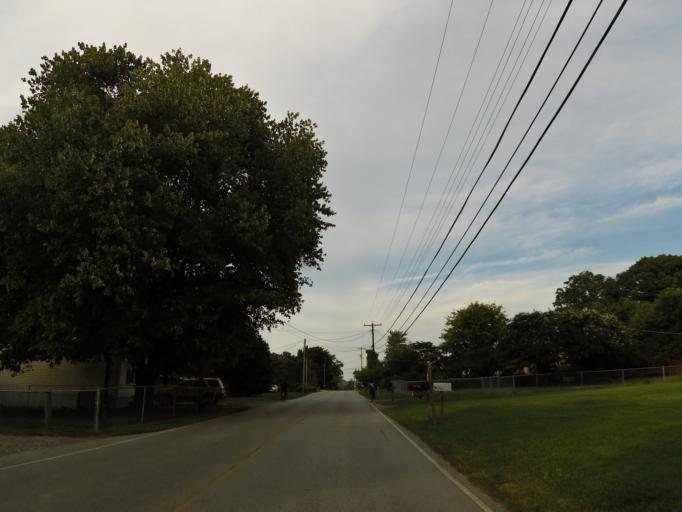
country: US
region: Tennessee
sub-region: Blount County
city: Alcoa
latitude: 35.8145
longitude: -83.9593
